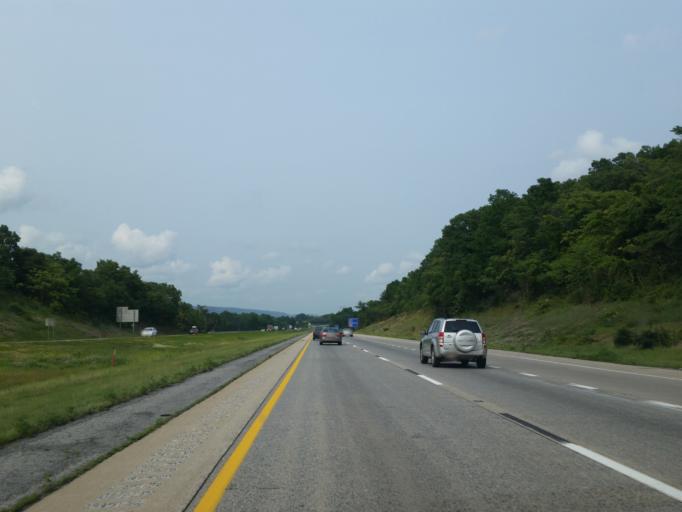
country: US
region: Pennsylvania
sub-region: Dauphin County
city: Skyline View
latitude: 40.3561
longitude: -76.7157
